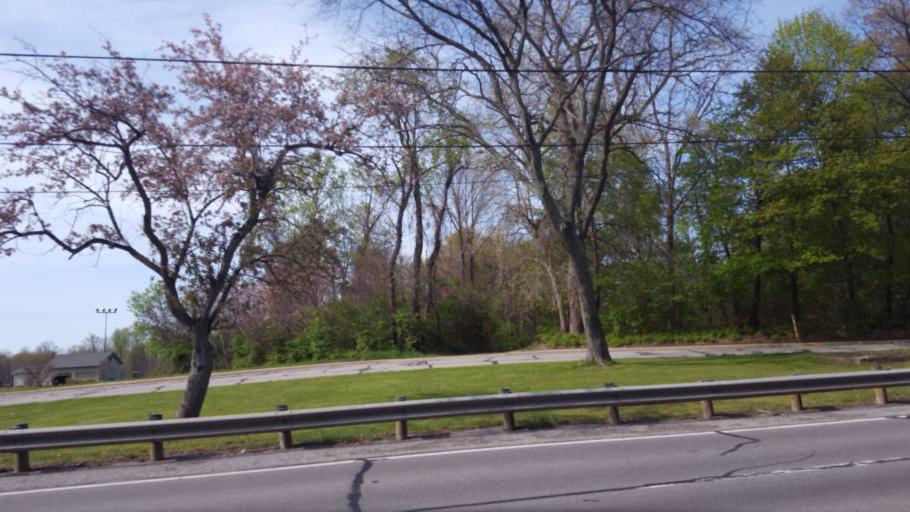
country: US
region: Ohio
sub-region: Lake County
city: Perry
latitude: 41.7854
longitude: -81.1355
